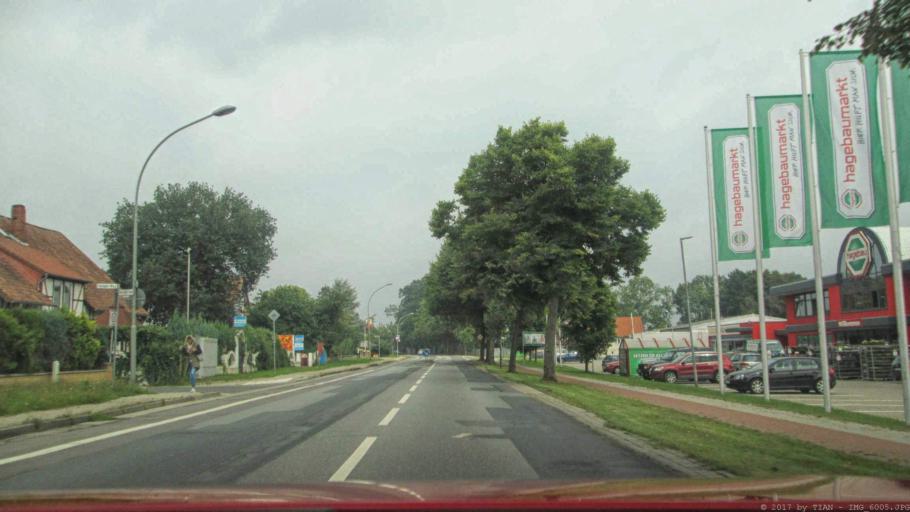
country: DE
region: Lower Saxony
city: Gifhorn
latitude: 52.5004
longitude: 10.5421
